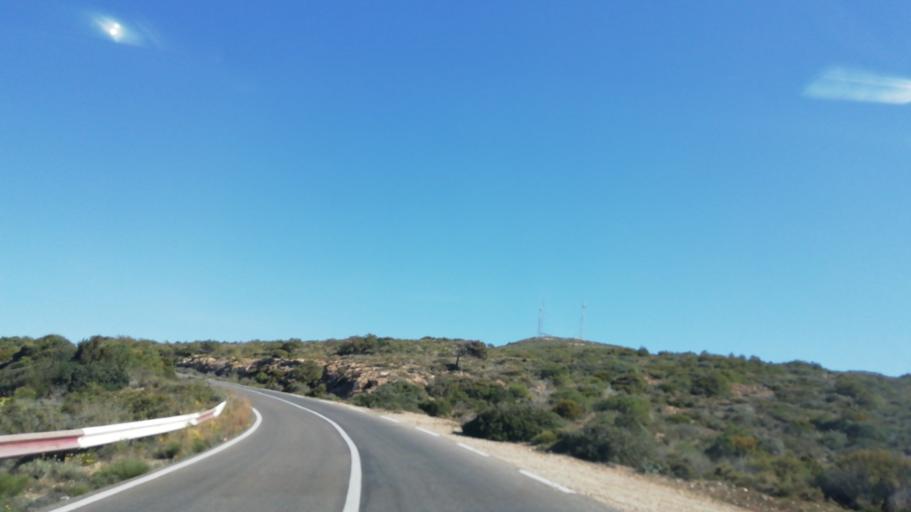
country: DZ
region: Ain Temouchent
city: El Amria
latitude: 35.6483
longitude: -1.0413
